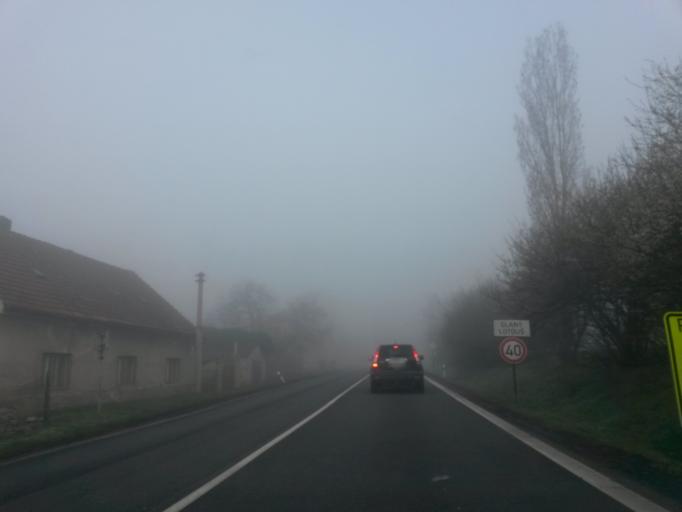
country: CZ
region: Central Bohemia
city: Klobuky
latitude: 50.2527
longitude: 14.0303
